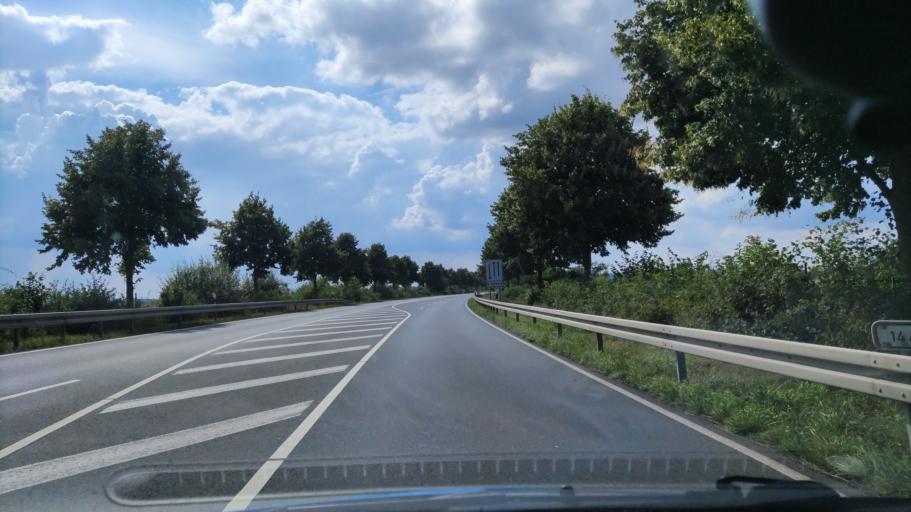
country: DE
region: Lower Saxony
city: Pattensen
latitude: 52.2480
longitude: 9.7755
